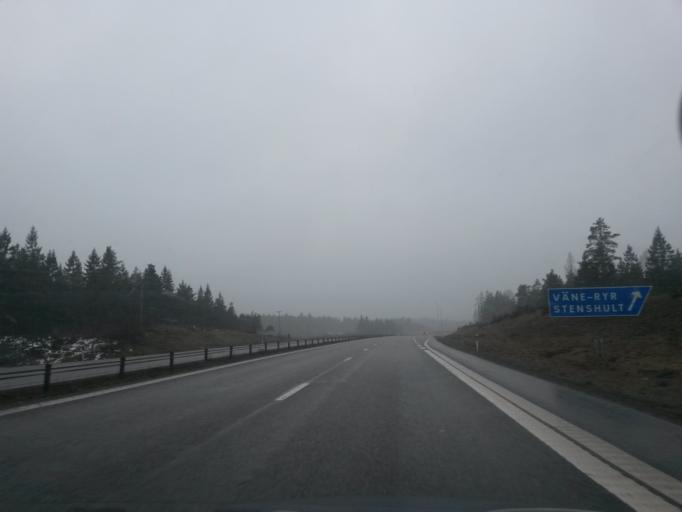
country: SE
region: Vaestra Goetaland
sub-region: Trollhattan
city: Trollhattan
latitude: 58.3264
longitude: 12.1666
